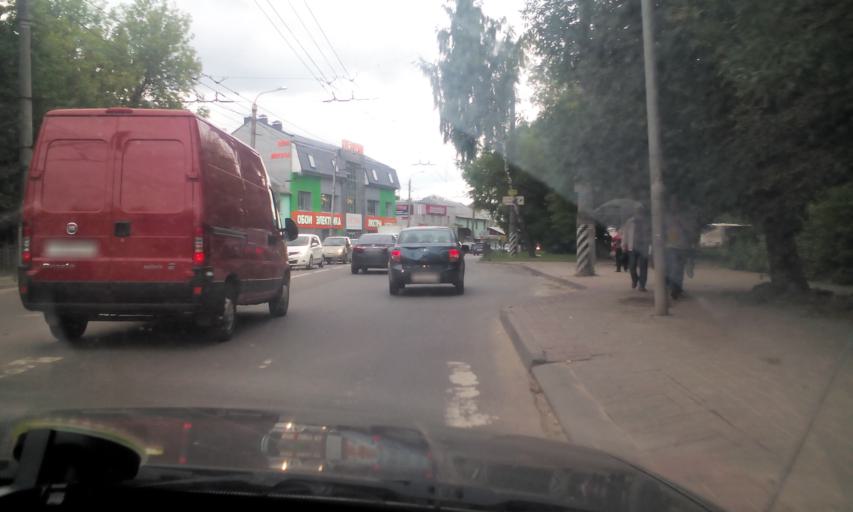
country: RU
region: Kaluga
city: Kaluga
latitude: 54.5389
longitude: 36.2778
